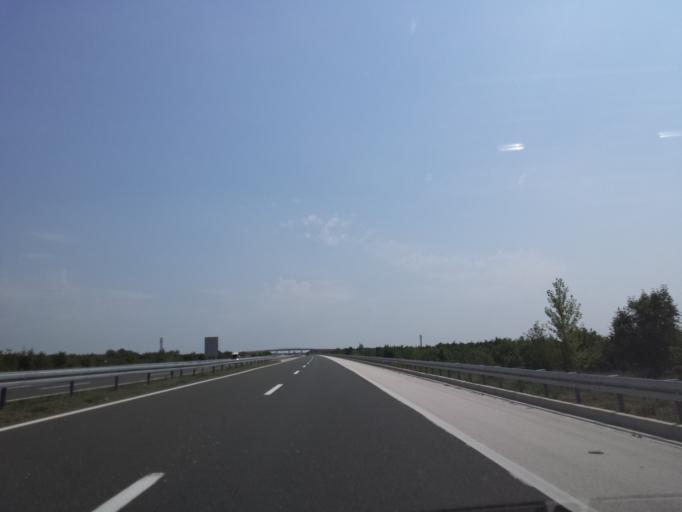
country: HR
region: Sibensko-Kniniska
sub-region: Grad Sibenik
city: Pirovac
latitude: 43.9314
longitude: 15.7143
